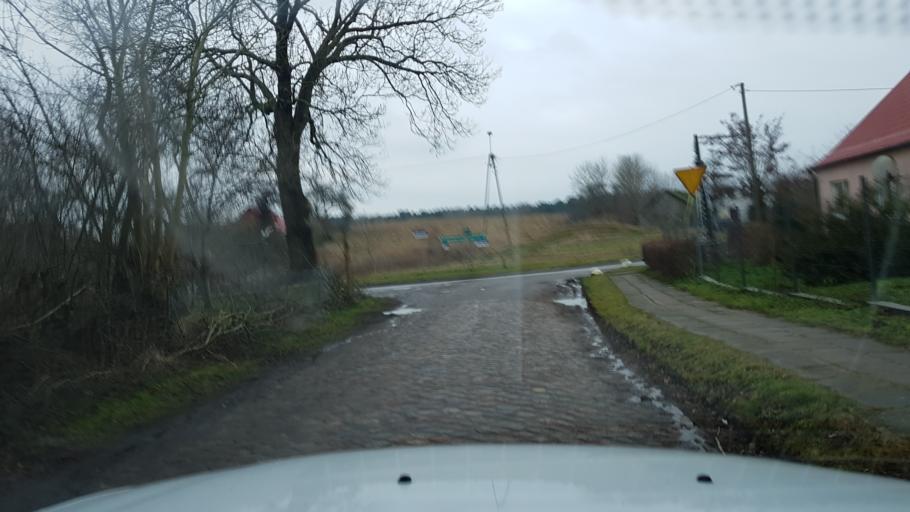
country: PL
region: West Pomeranian Voivodeship
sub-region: Powiat kolobrzeski
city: Grzybowo
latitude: 54.1331
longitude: 15.4823
